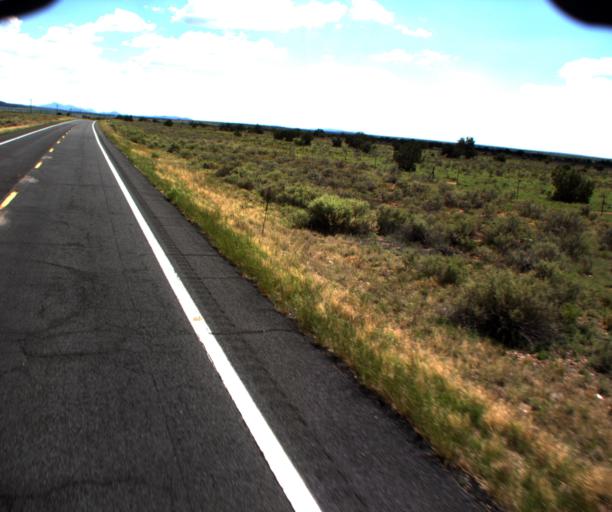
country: US
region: Arizona
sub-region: Coconino County
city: Williams
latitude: 35.6046
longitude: -112.1462
